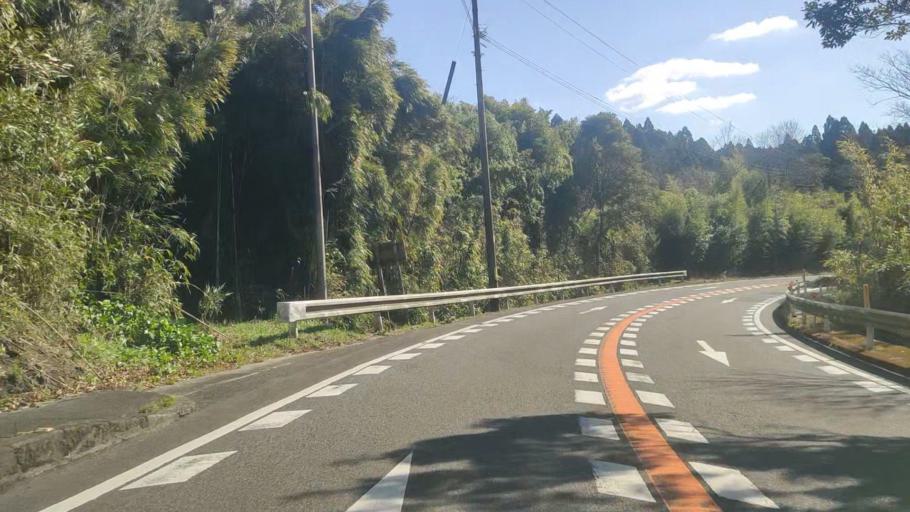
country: JP
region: Kagoshima
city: Kokubu-matsuki
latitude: 31.6659
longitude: 130.8804
